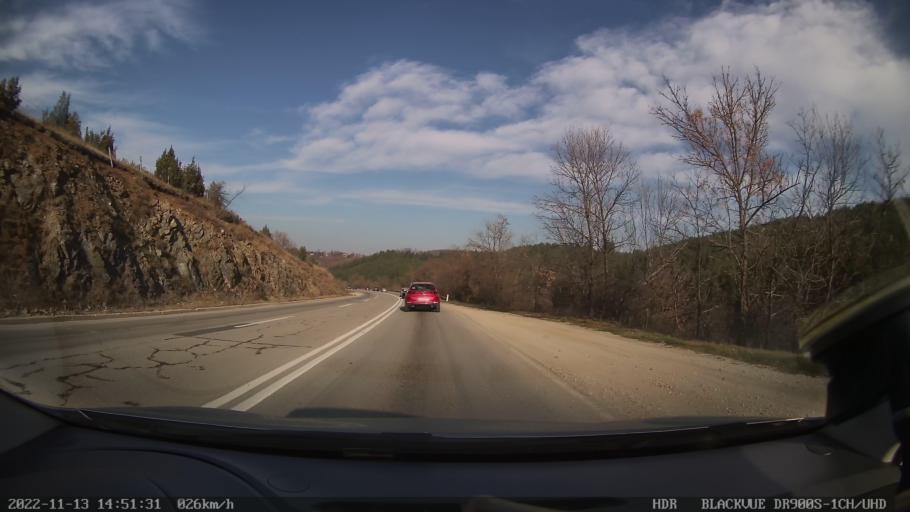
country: RS
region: Central Serbia
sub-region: Zlatiborski Okrug
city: Cajetina
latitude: 43.7673
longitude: 19.7359
